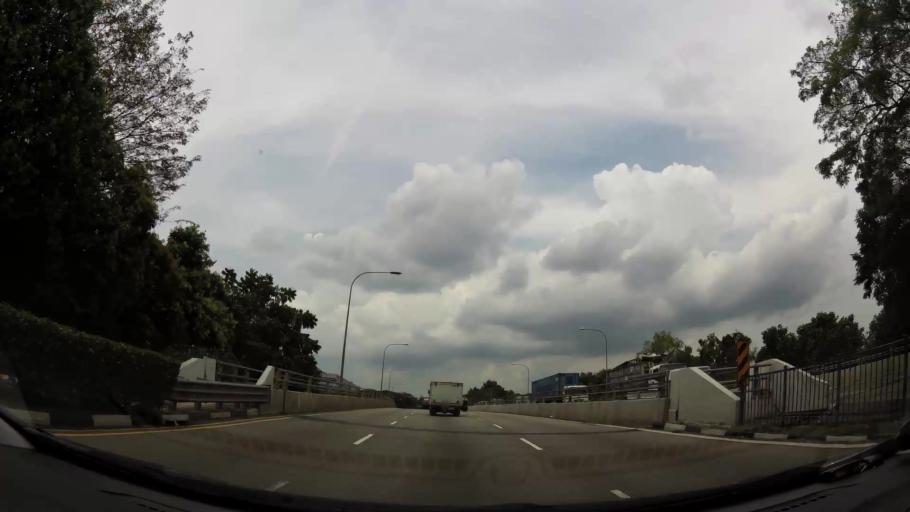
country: SG
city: Singapore
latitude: 1.3227
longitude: 103.7642
